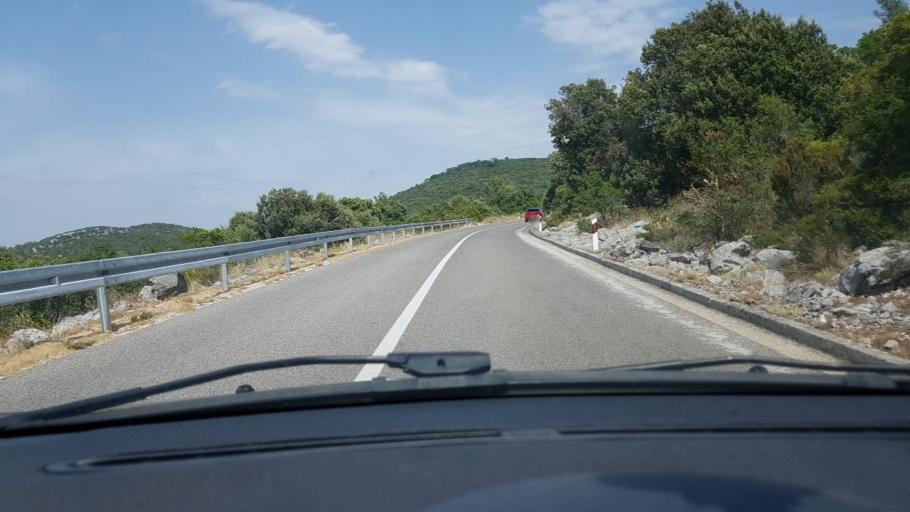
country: HR
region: Dubrovacko-Neretvanska
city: Smokvica
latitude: 42.9490
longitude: 16.9700
